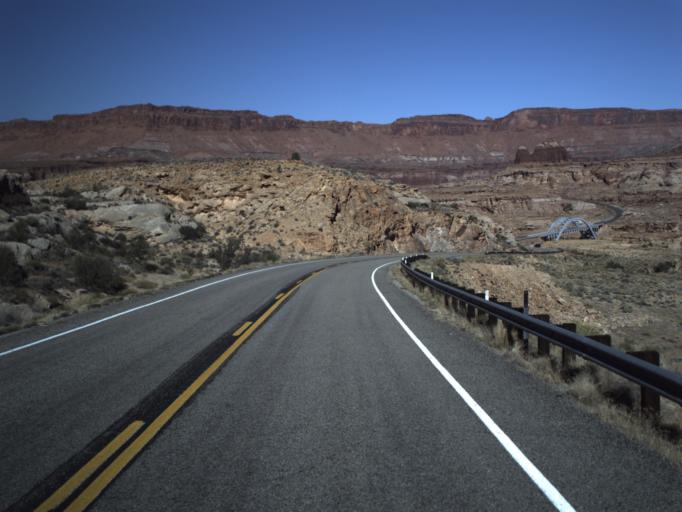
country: US
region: Utah
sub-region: San Juan County
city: Blanding
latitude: 37.8854
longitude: -110.3642
